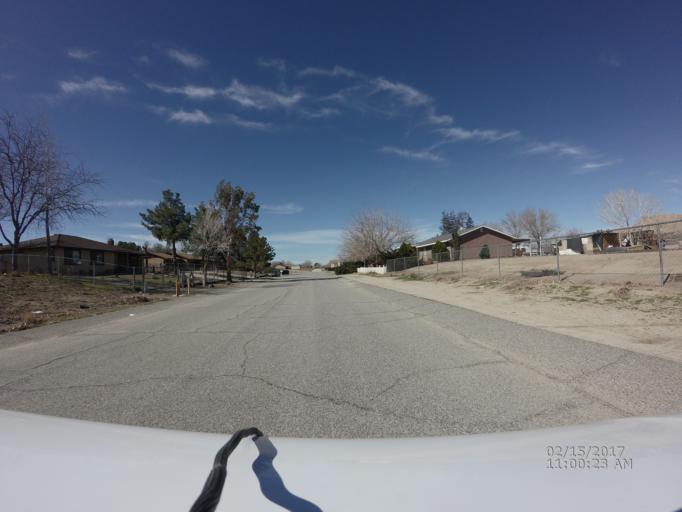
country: US
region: California
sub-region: Los Angeles County
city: Lake Los Angeles
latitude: 34.5813
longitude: -117.8505
